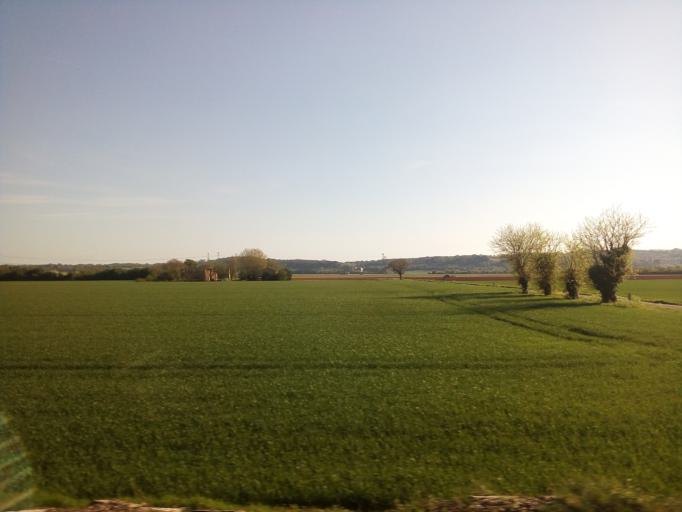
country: FR
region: Rhone-Alpes
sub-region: Departement du Rhone
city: Saint-Laurent-de-Mure
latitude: 45.6600
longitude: 5.0453
